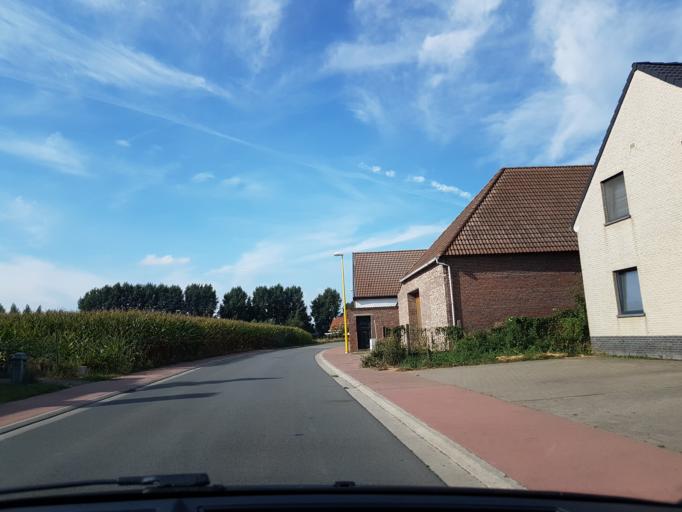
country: BE
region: Flanders
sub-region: Provincie Vlaams-Brabant
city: Grimbergen
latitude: 50.9562
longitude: 4.3928
